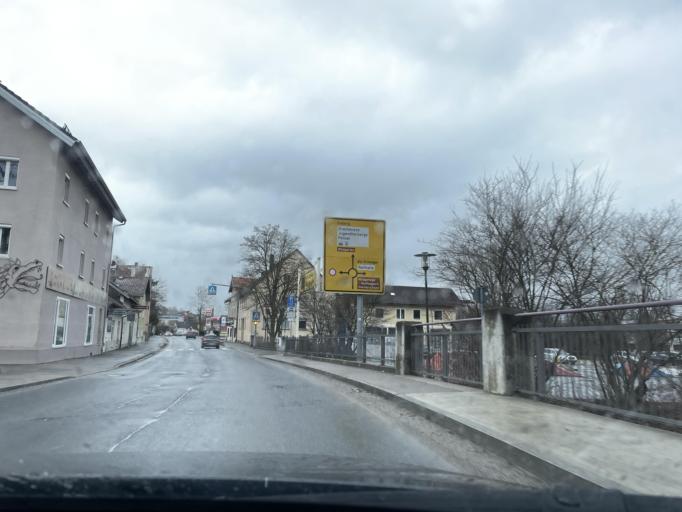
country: DE
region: Bavaria
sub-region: Upper Palatinate
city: Furth im Wald
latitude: 49.3057
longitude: 12.8477
